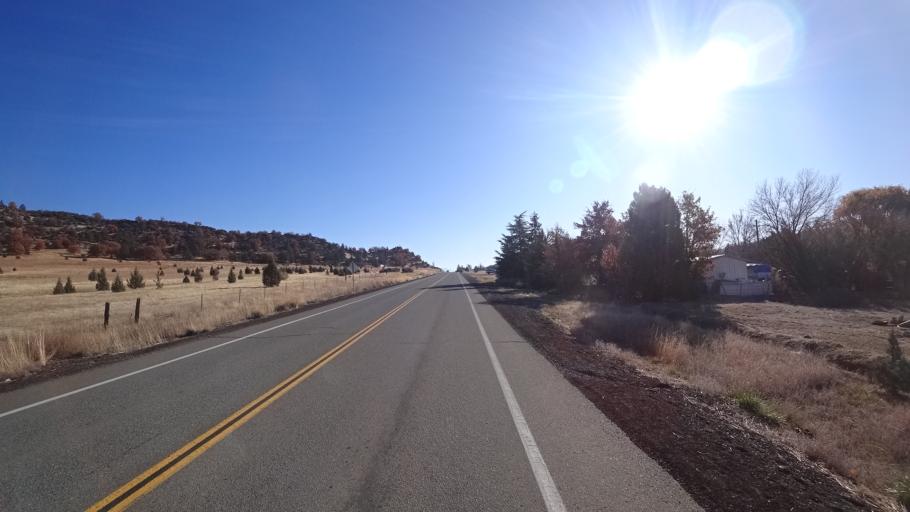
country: US
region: California
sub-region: Siskiyou County
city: Yreka
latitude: 41.7134
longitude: -122.6221
